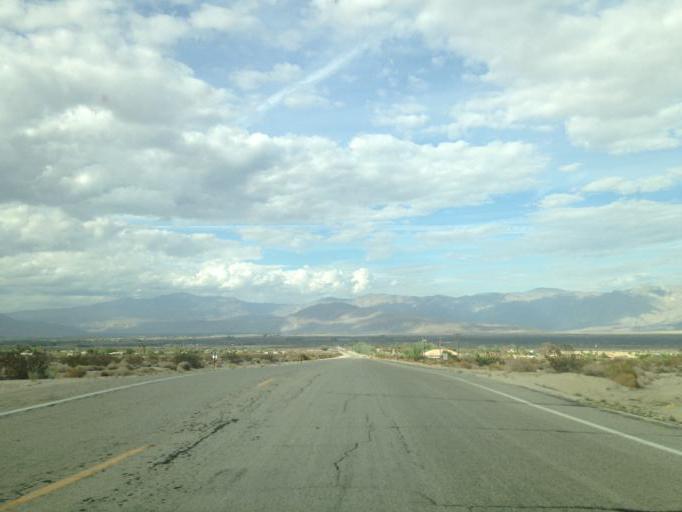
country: US
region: California
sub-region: San Diego County
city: Borrego Springs
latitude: 33.1983
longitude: -116.3303
